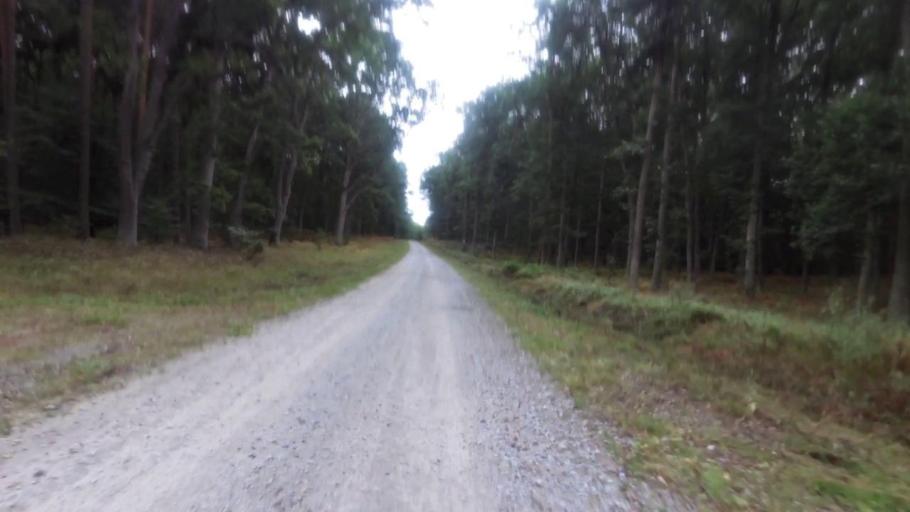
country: PL
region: Lubusz
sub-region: Powiat gorzowski
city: Kostrzyn nad Odra
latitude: 52.6416
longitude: 14.6432
